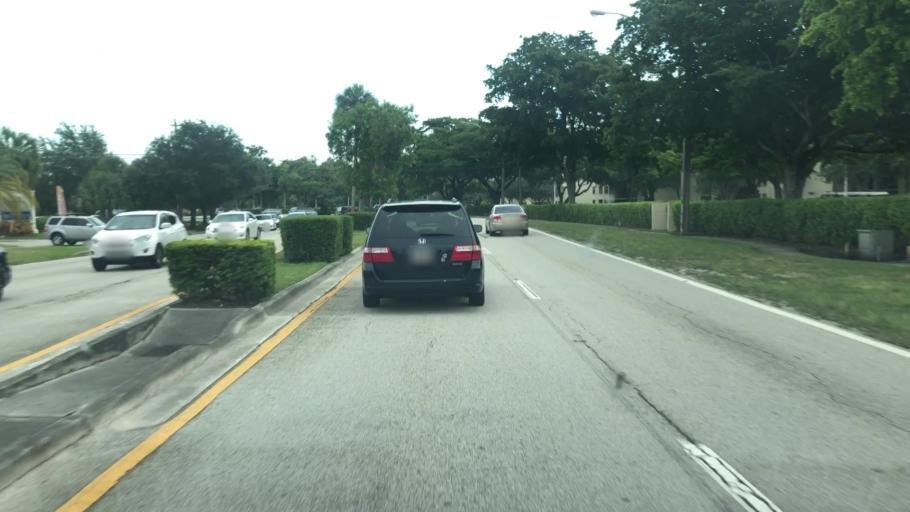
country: US
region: Florida
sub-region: Broward County
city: Tedder
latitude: 26.3011
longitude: -80.1326
